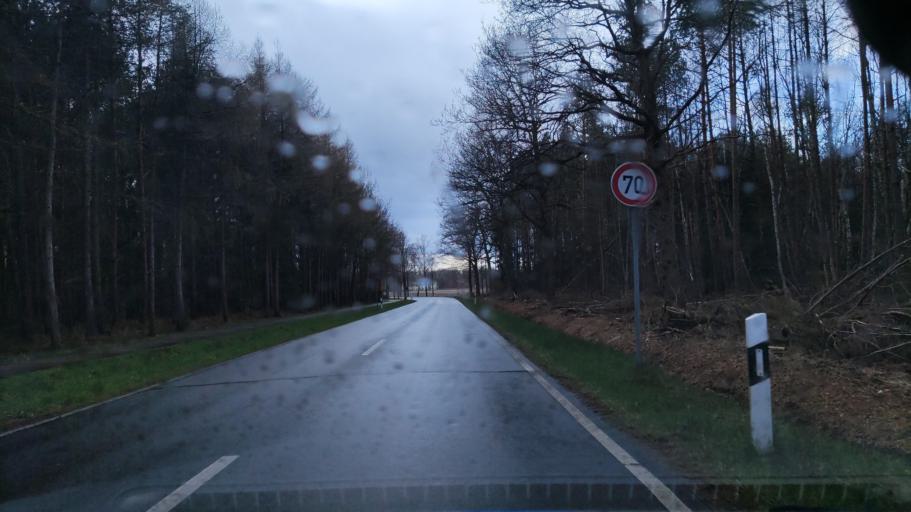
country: DE
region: Lower Saxony
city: Hermannsburg
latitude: 52.8317
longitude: 10.1125
